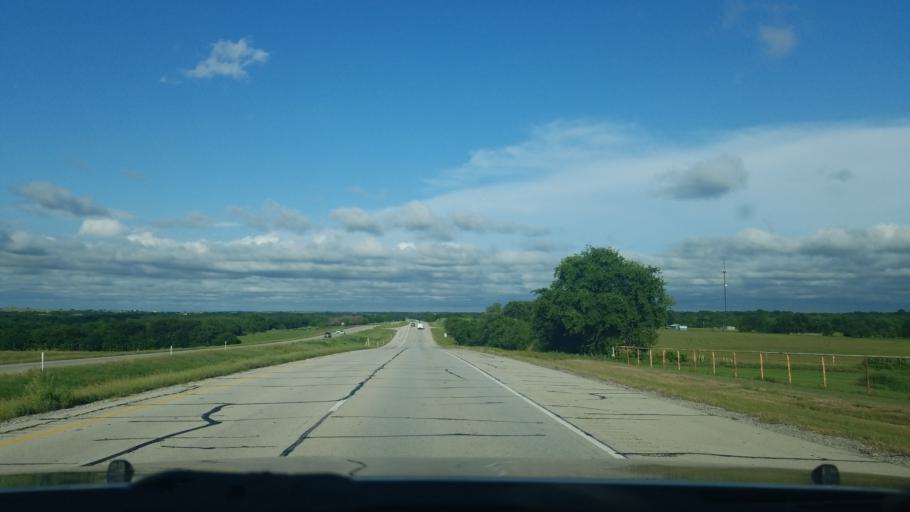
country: US
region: Texas
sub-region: Wise County
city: Decatur
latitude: 33.2450
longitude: -97.4766
